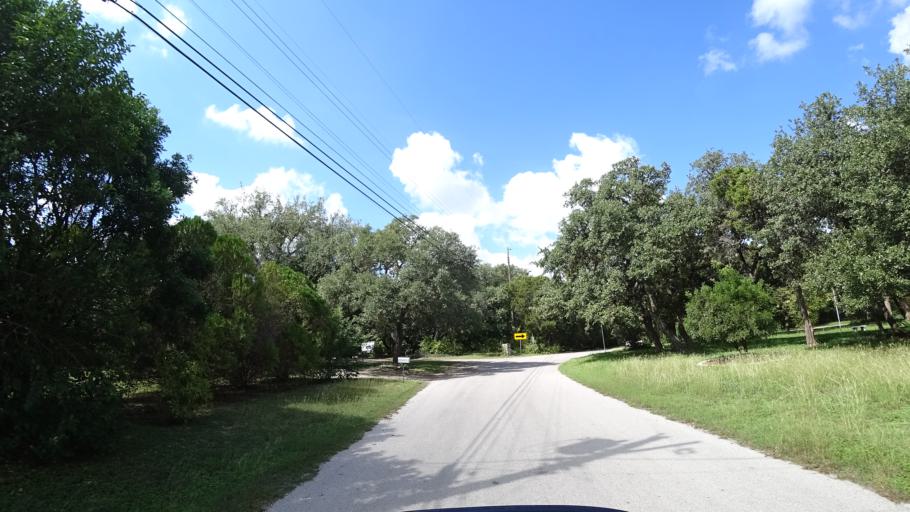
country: US
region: Texas
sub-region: Travis County
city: Onion Creek
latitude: 30.1898
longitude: -97.8000
